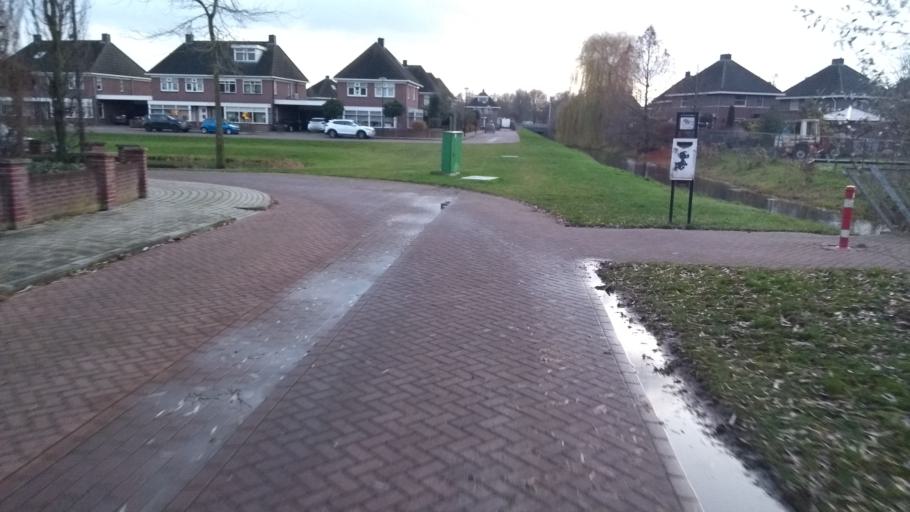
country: NL
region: Overijssel
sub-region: Gemeente Almelo
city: Almelo
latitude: 52.3754
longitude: 6.6918
